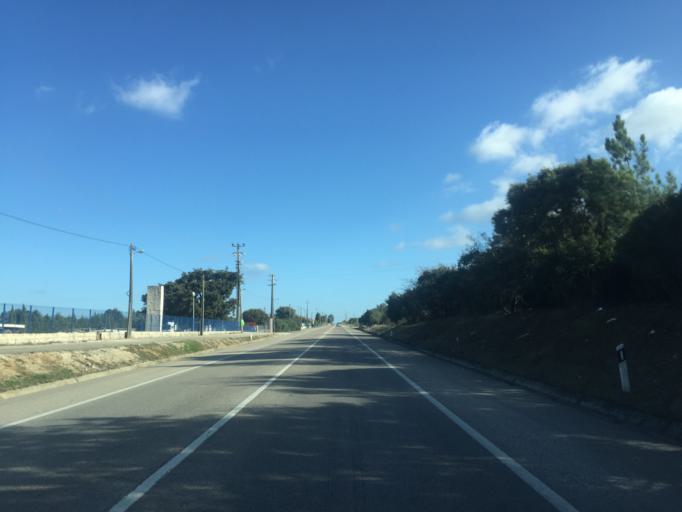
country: PT
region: Leiria
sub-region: Alcobaca
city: Aljubarrota
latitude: 39.5191
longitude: -8.9158
